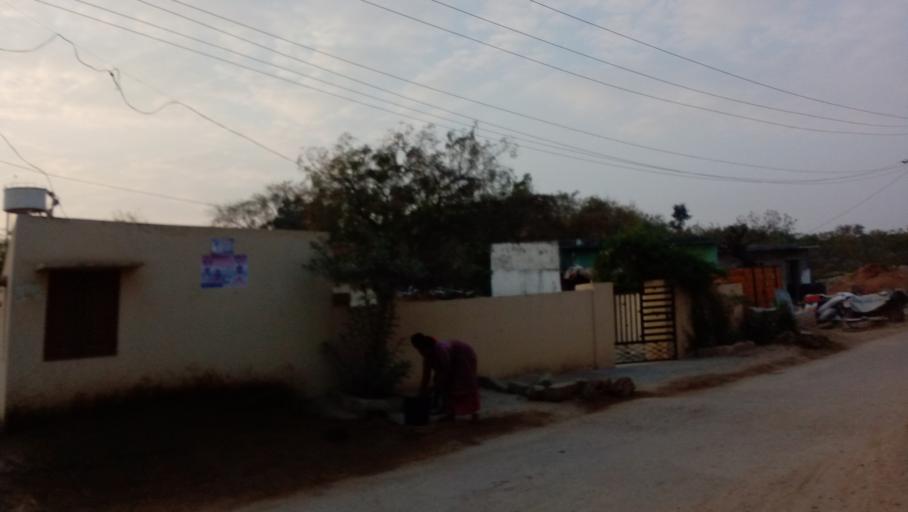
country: IN
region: Telangana
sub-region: Medak
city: Serilingampalle
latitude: 17.5187
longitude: 78.3087
